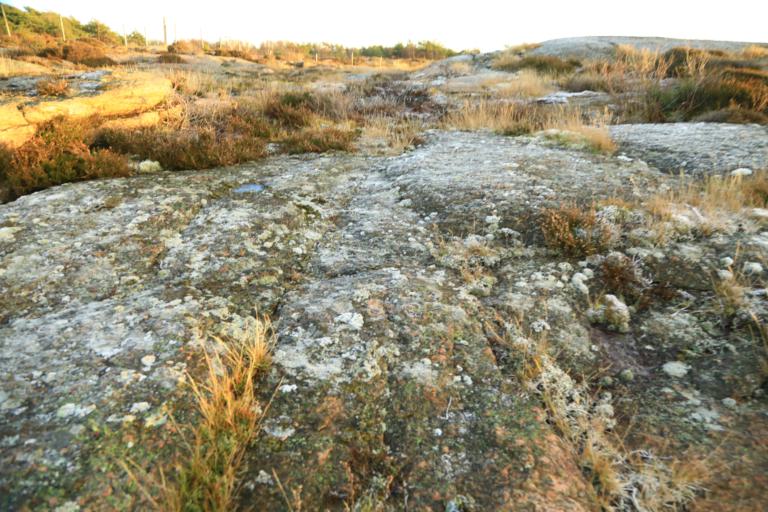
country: SE
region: Halland
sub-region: Kungsbacka Kommun
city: Frillesas
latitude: 57.1927
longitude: 12.1613
